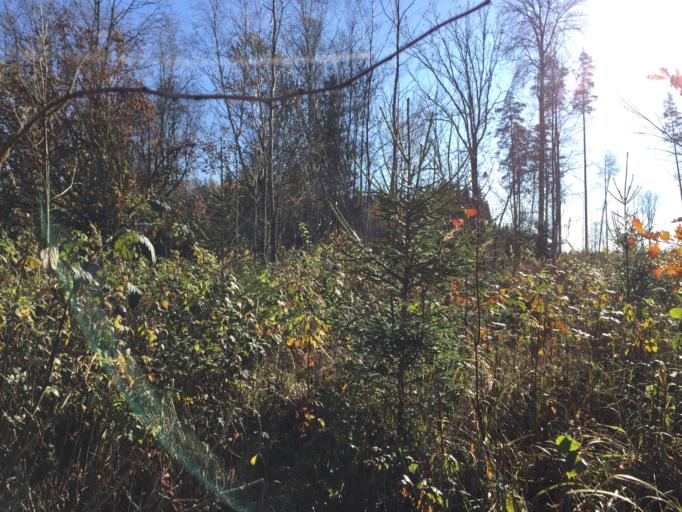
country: LV
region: Aizkraukles Rajons
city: Aizkraukle
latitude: 56.5728
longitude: 25.1835
